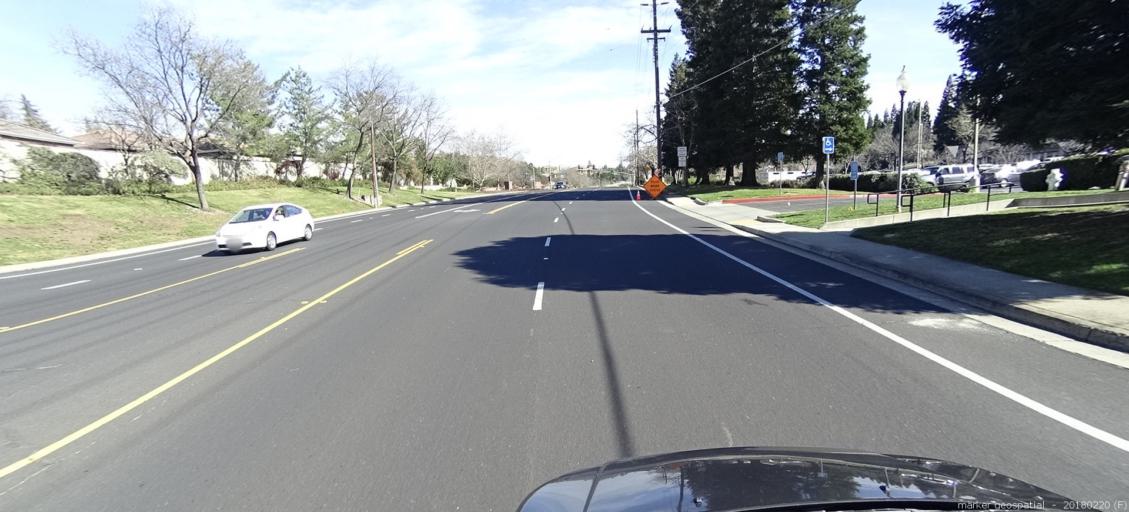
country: US
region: California
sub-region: Sacramento County
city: Folsom
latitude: 38.6996
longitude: -121.1918
